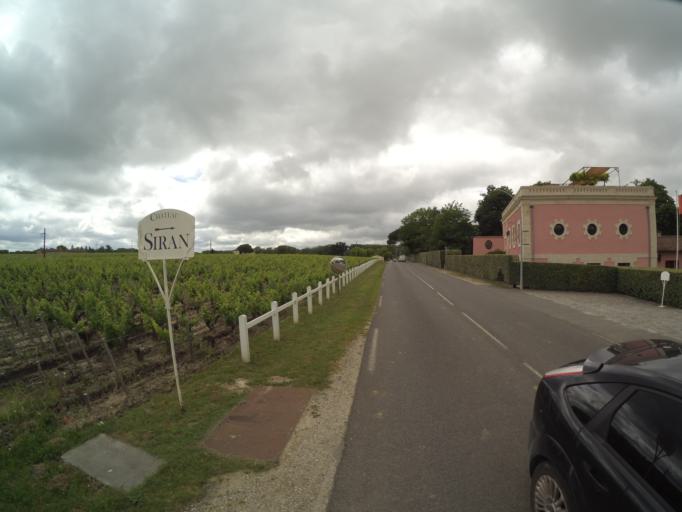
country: FR
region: Aquitaine
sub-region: Departement de la Gironde
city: Cantenac
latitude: 45.0217
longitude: -0.6345
